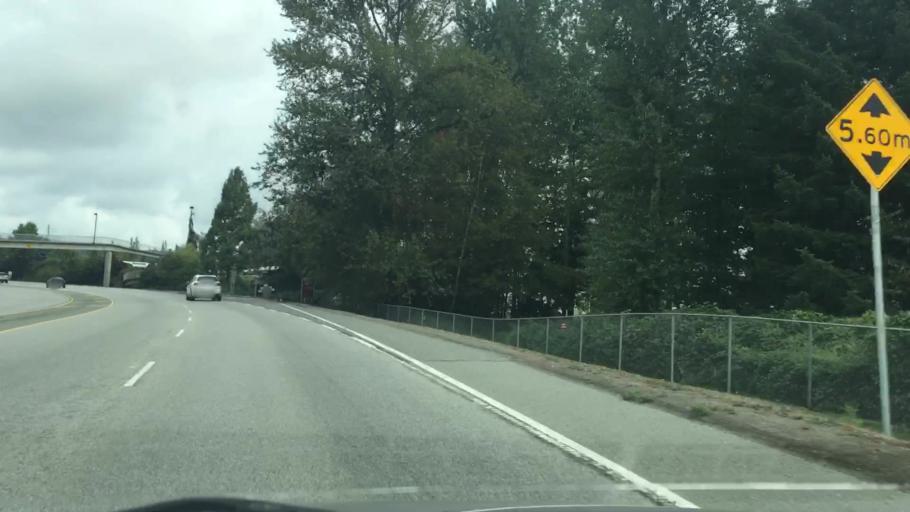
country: CA
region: British Columbia
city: Langley
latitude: 49.1090
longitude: -122.6427
